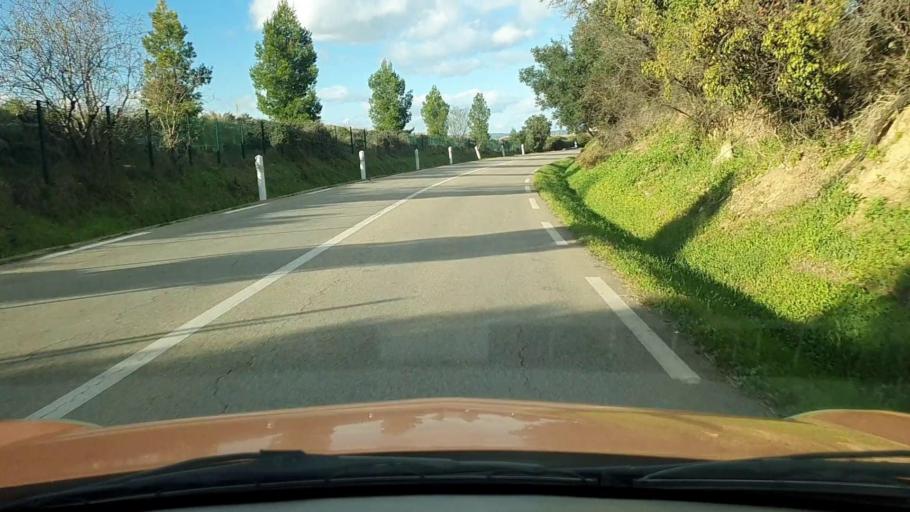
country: FR
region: Languedoc-Roussillon
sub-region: Departement du Gard
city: Vauvert
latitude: 43.6839
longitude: 4.2738
